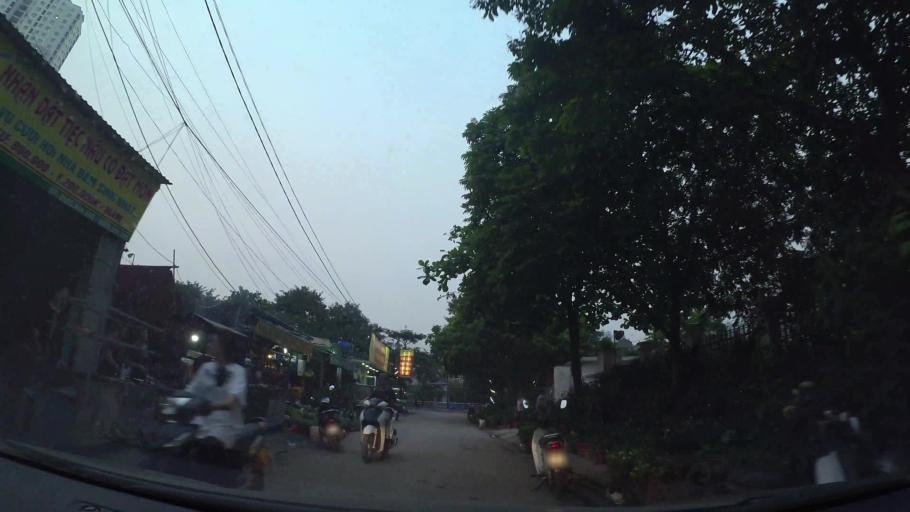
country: VN
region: Ha Noi
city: Ha Dong
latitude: 20.9694
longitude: 105.7868
